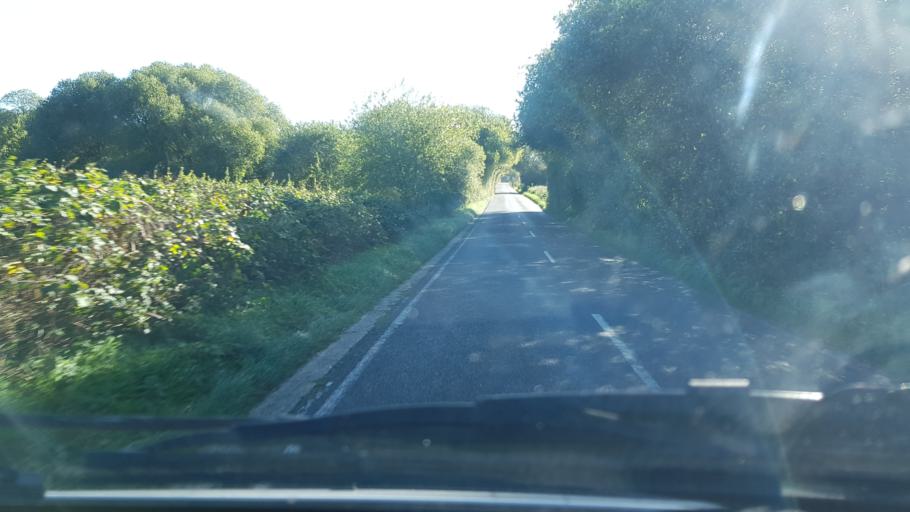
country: GB
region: England
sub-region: Surrey
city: Cranleigh
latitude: 51.1621
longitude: -0.5001
